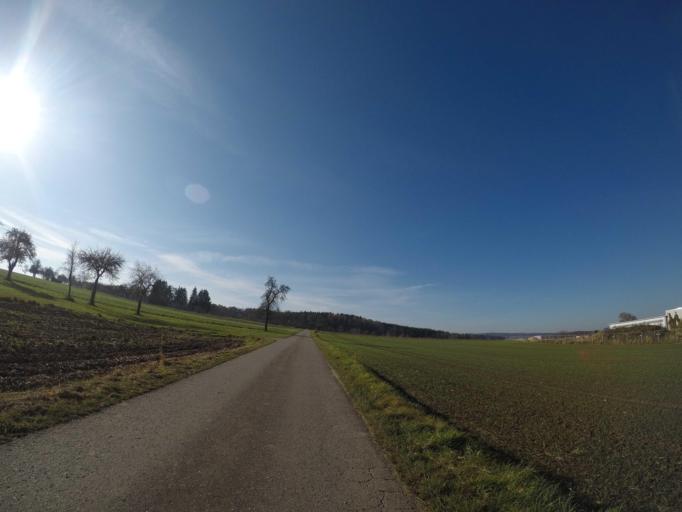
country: DE
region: Baden-Wuerttemberg
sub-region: Tuebingen Region
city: Obermarchtal
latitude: 48.2266
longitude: 9.5669
